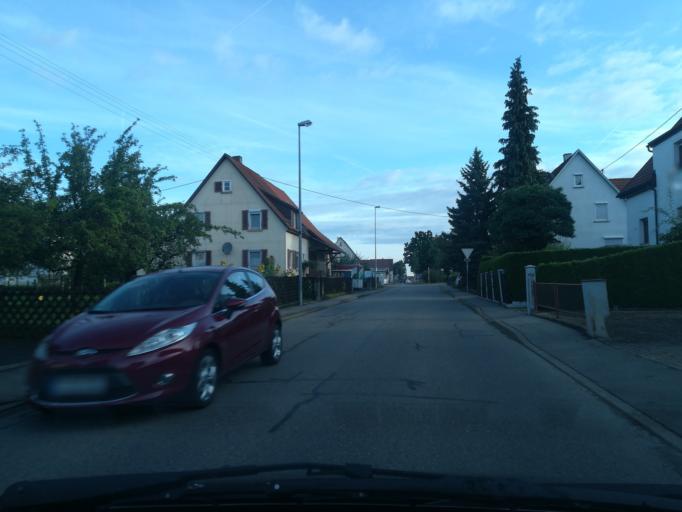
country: DE
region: Baden-Wuerttemberg
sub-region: Tuebingen Region
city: Sickenhausen
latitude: 48.5180
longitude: 9.1760
